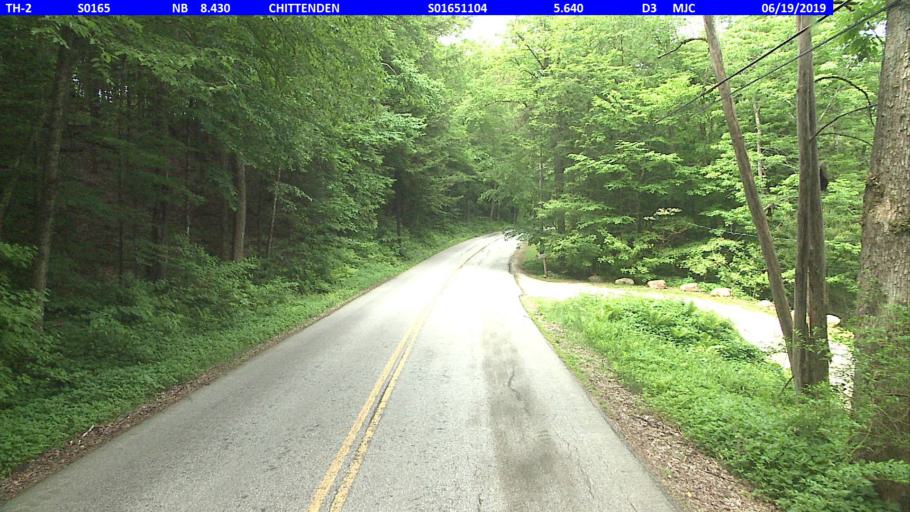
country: US
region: Vermont
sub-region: Rutland County
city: Rutland
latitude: 43.7323
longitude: -72.9842
